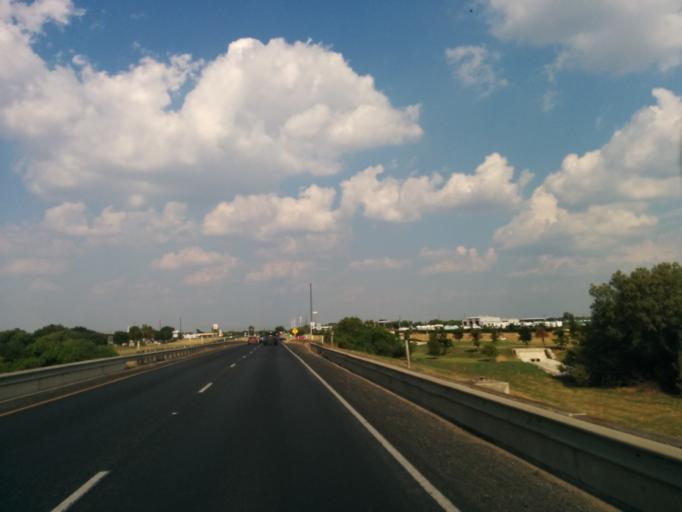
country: US
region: Texas
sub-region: Bexar County
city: Elmendorf
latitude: 29.3075
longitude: -98.3992
